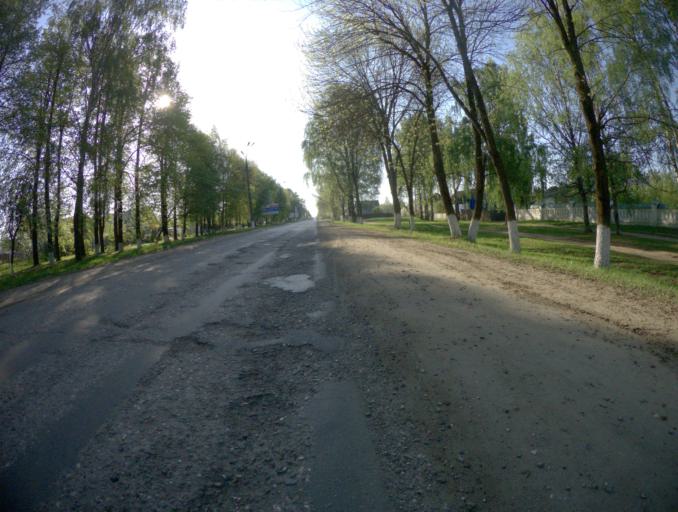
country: RU
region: Vladimir
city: Vyazniki
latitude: 56.2379
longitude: 42.1758
